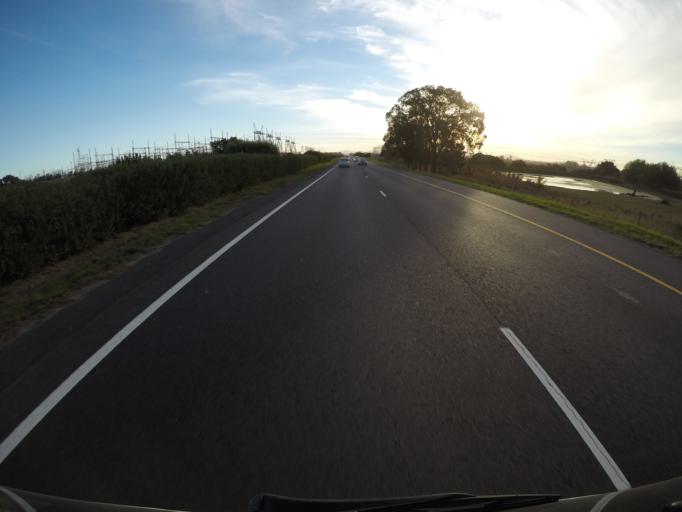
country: ZA
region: Western Cape
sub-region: City of Cape Town
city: Kraaifontein
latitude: -33.8146
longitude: 18.8101
